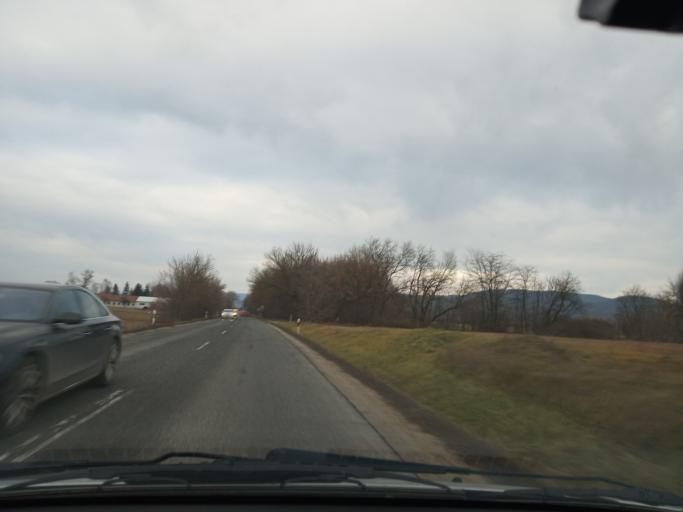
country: HU
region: Komarom-Esztergom
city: Esztergom
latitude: 47.7586
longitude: 18.7351
